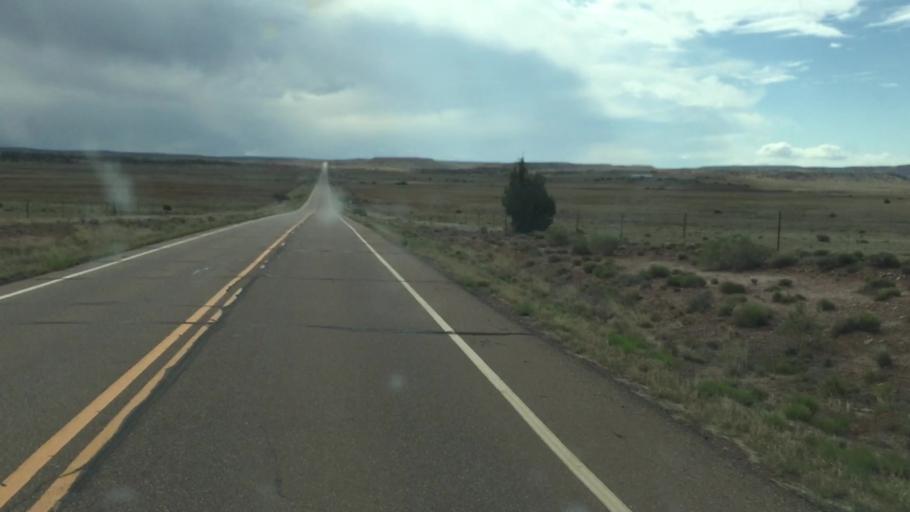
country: US
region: Arizona
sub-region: Apache County
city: Saint Johns
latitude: 34.5102
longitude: -109.6840
